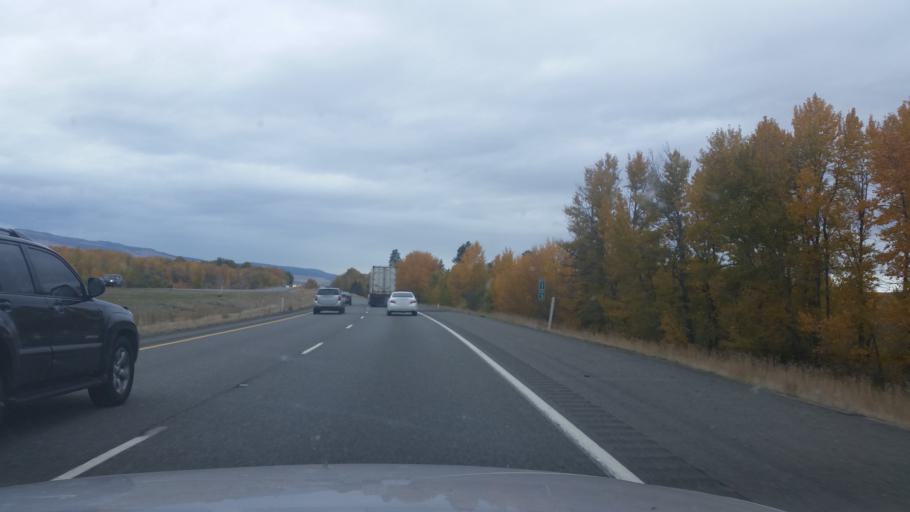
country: US
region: Washington
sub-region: Kittitas County
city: Ellensburg
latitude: 47.0405
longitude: -120.6299
